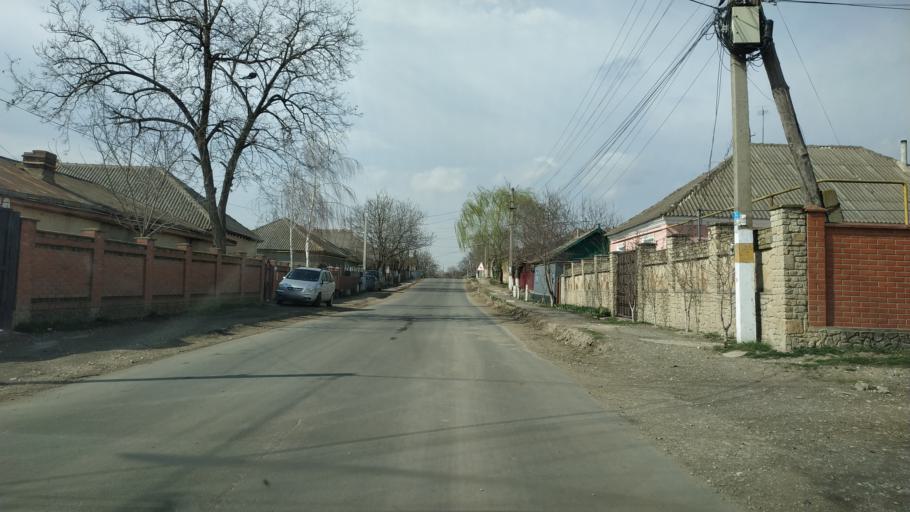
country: MD
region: Gagauzia
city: Vulcanesti
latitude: 45.6766
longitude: 28.4149
